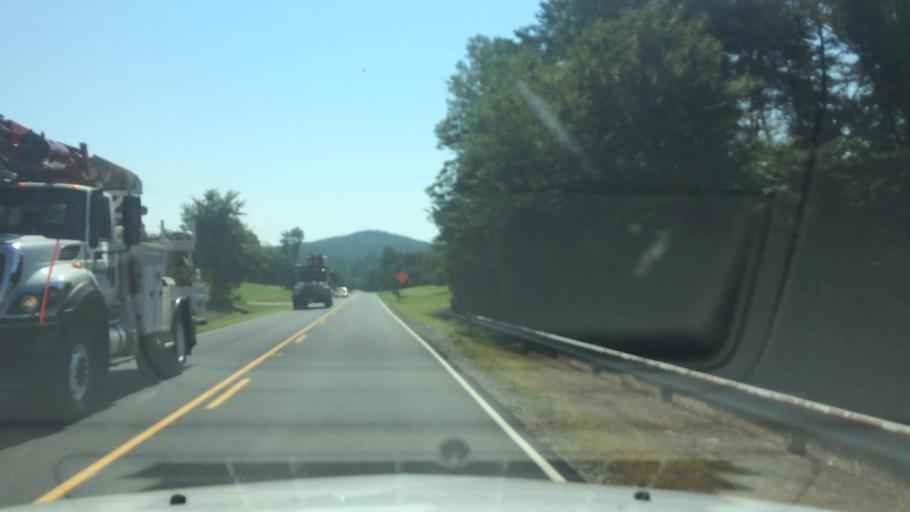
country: US
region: North Carolina
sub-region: Caldwell County
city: Sawmills
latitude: 35.9073
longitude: -81.4006
